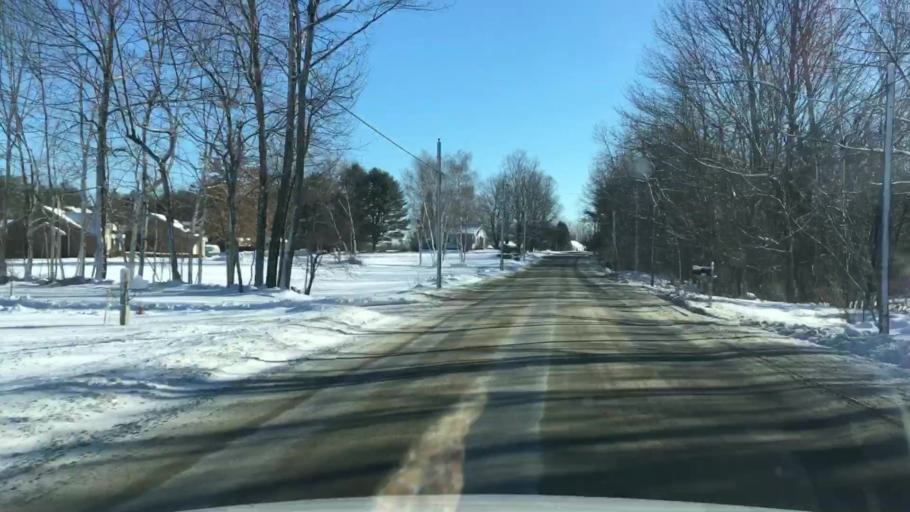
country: US
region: Maine
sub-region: Kennebec County
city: Winthrop
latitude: 44.3349
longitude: -69.9871
